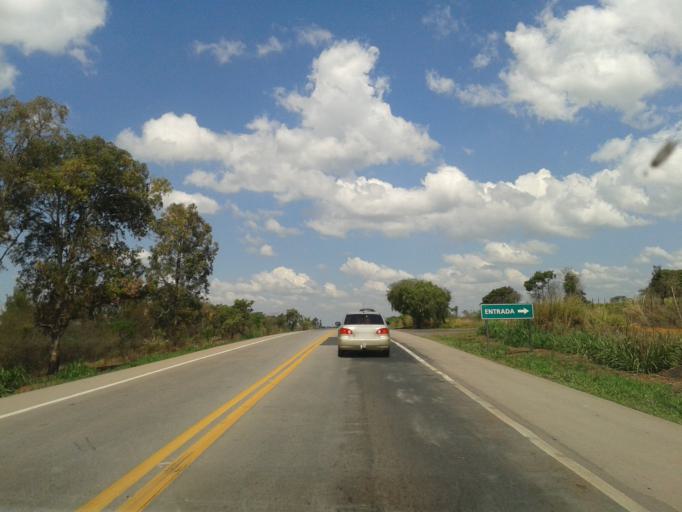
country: BR
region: Minas Gerais
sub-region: Campos Altos
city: Campos Altos
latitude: -19.6967
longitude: -46.0319
